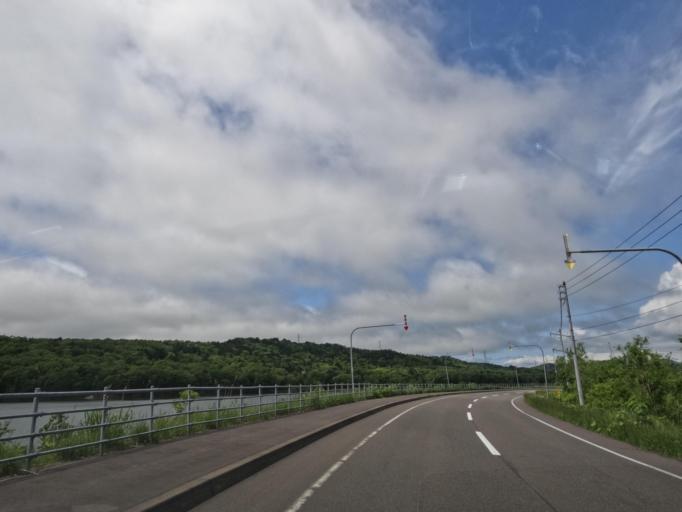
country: JP
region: Hokkaido
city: Tobetsu
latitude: 43.3569
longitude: 141.5681
